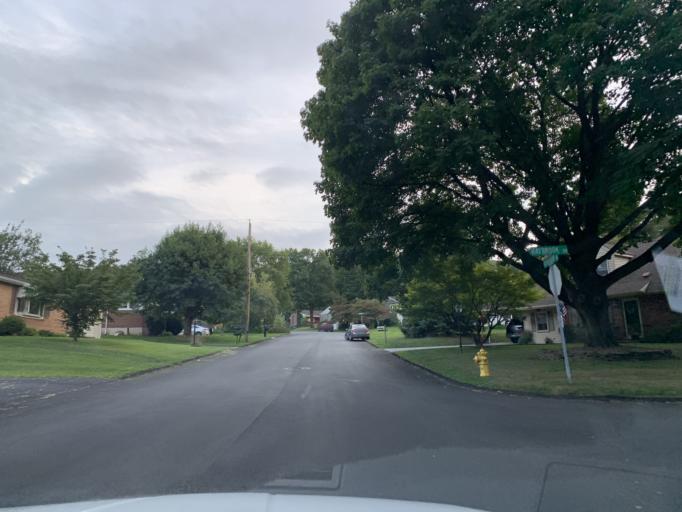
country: US
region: Pennsylvania
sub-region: York County
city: Emigsville
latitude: 40.0053
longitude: -76.7271
